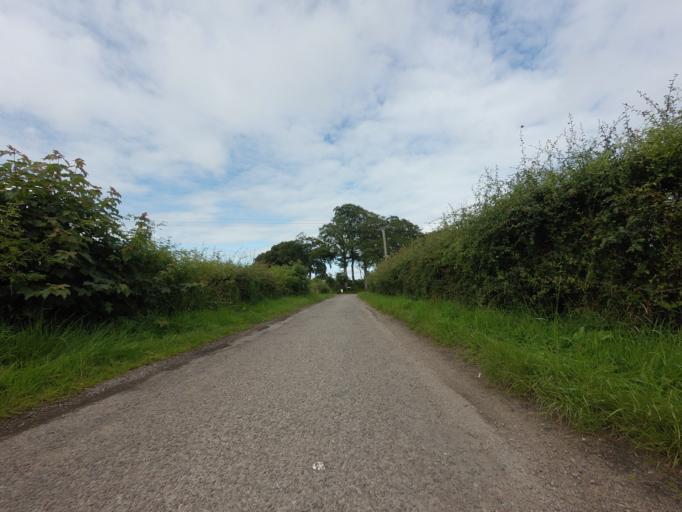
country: GB
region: Scotland
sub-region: Moray
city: Hopeman
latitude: 57.6703
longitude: -3.3960
